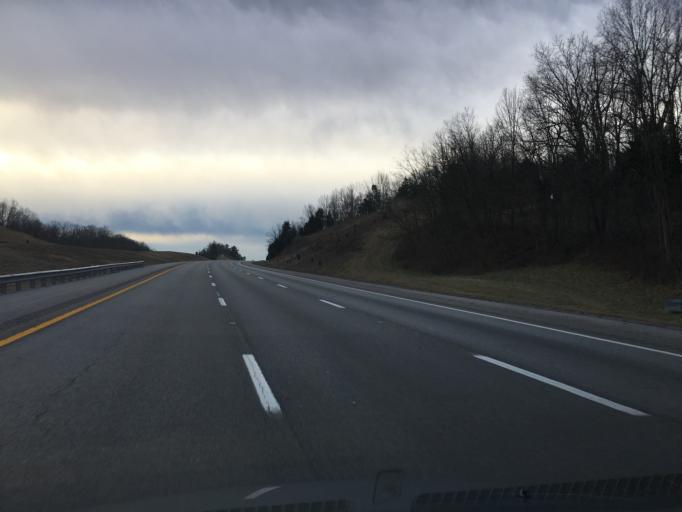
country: US
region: Kentucky
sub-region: Grant County
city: Williamstown
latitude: 38.4659
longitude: -84.5780
